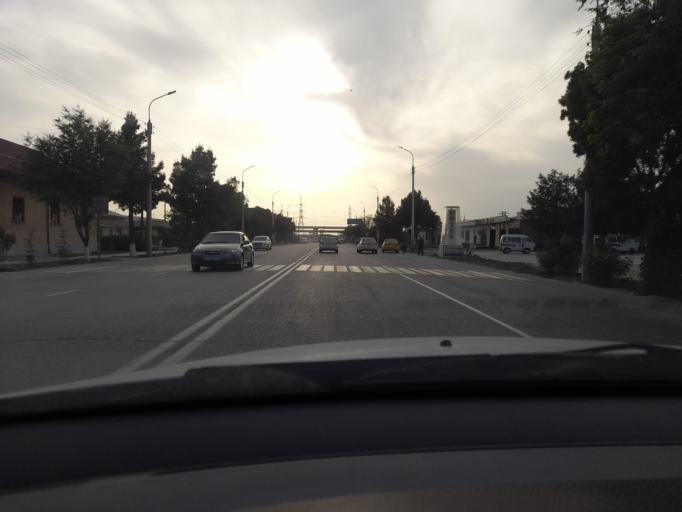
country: UZ
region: Navoiy
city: Beshrabot
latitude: 40.1480
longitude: 65.3208
